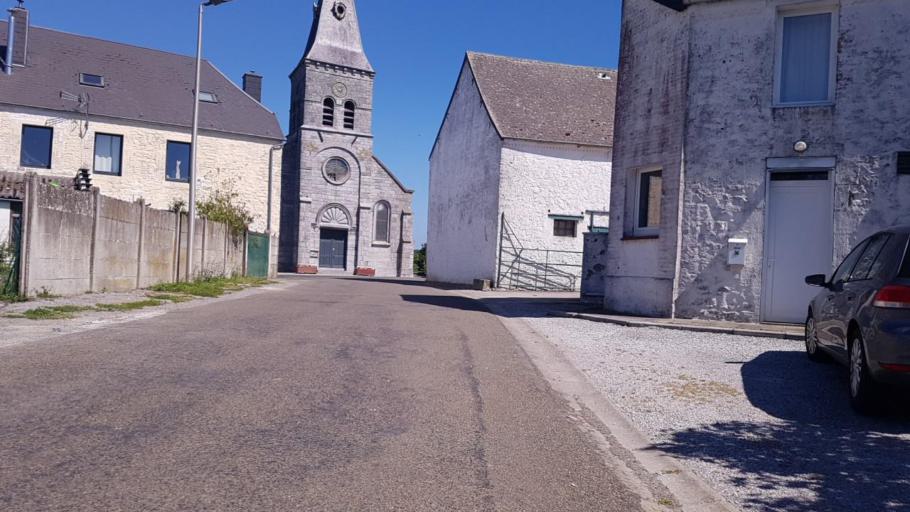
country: BE
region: Wallonia
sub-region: Province du Hainaut
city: Chimay
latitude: 50.0688
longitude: 4.2384
